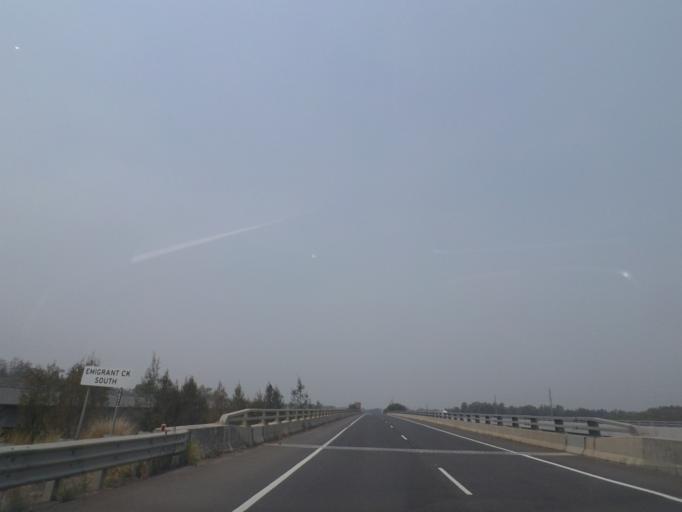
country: AU
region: New South Wales
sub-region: Ballina
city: Ballina
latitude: -28.8658
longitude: 153.5008
